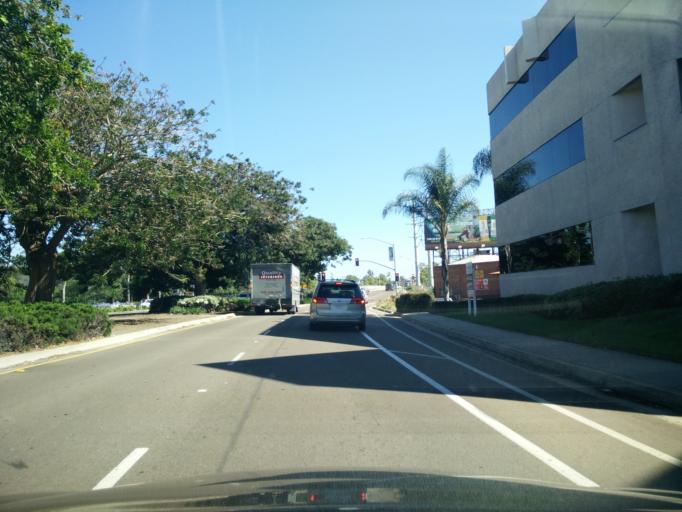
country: US
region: California
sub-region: San Diego County
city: San Diego
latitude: 32.7650
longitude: -117.1983
